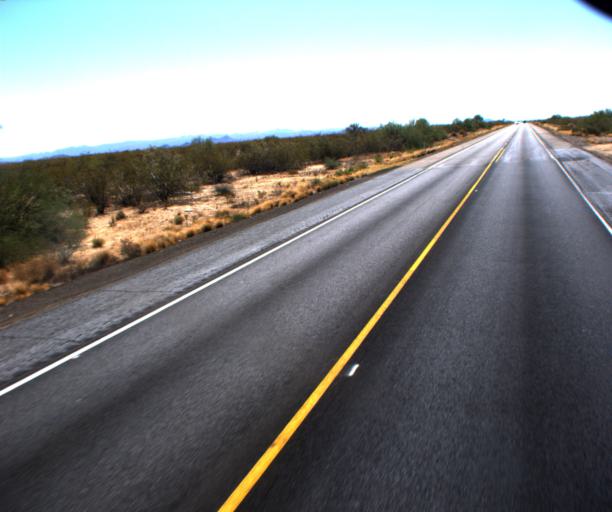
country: US
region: Arizona
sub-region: Yavapai County
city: Congress
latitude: 34.0523
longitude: -112.8485
